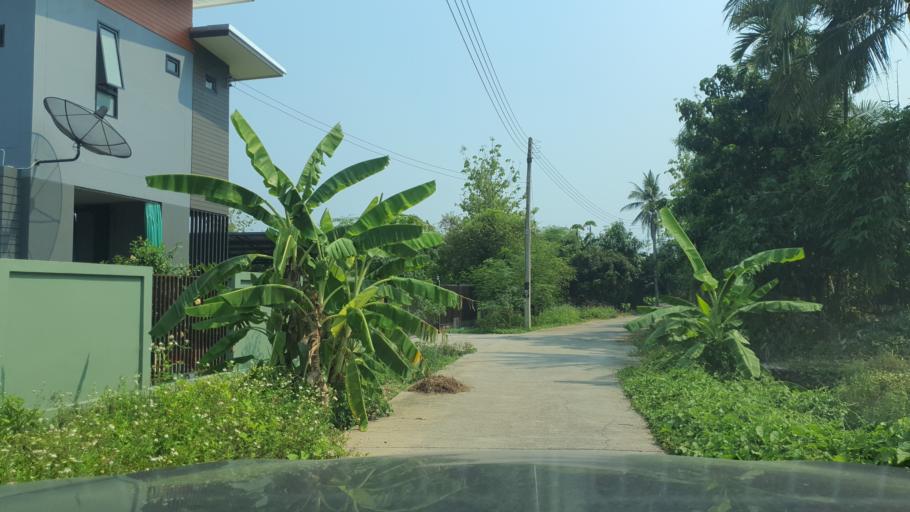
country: TH
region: Chiang Mai
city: Saraphi
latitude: 18.6562
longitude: 98.9881
